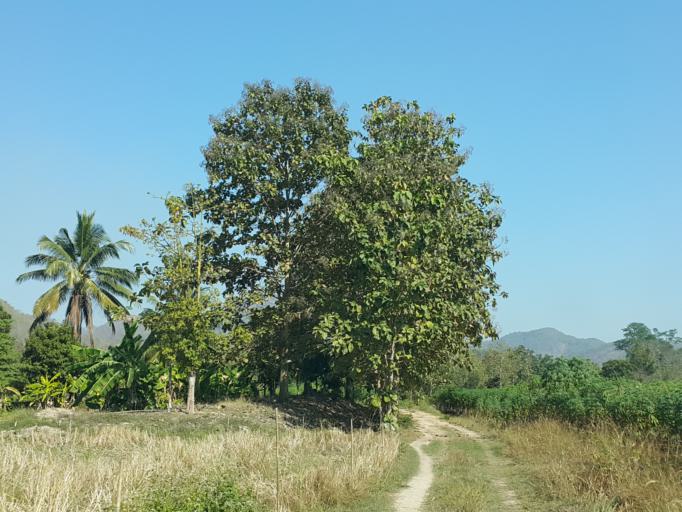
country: TH
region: Sukhothai
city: Thung Saliam
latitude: 17.3263
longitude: 99.4608
